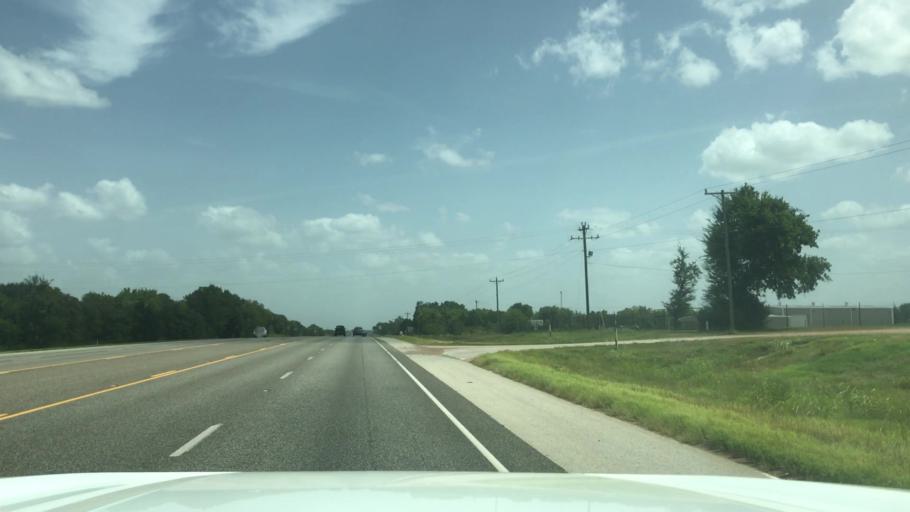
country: US
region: Texas
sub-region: Robertson County
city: Calvert
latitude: 30.9671
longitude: -96.6644
